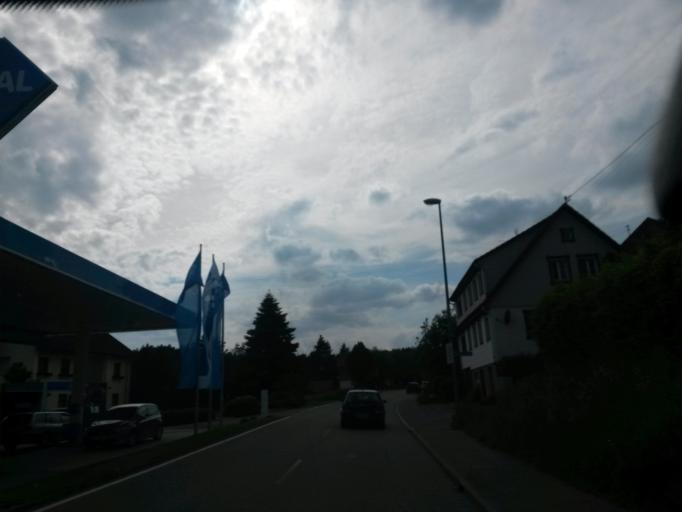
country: DE
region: Baden-Wuerttemberg
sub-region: Karlsruhe Region
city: Oberreichenbach
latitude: 48.7342
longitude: 8.6633
